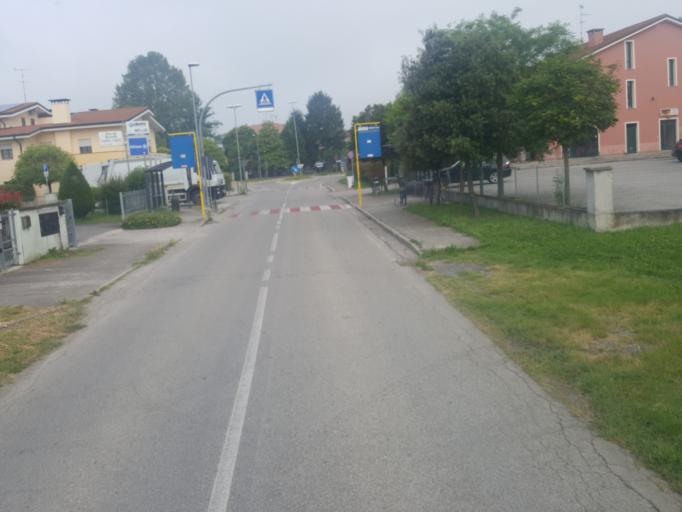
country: IT
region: Veneto
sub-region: Provincia di Rovigo
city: Canaro
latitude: 44.9319
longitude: 11.6772
